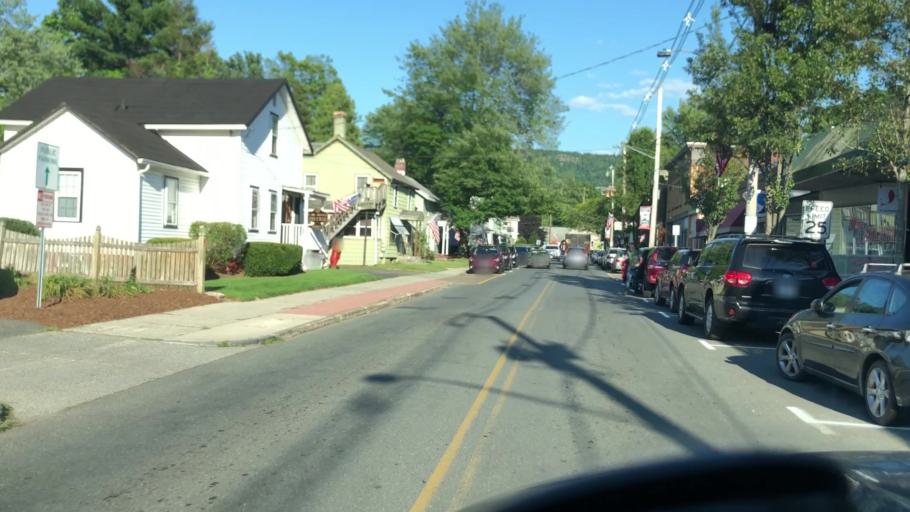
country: US
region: Massachusetts
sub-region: Hampshire County
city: Easthampton
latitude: 42.2645
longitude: -72.6655
